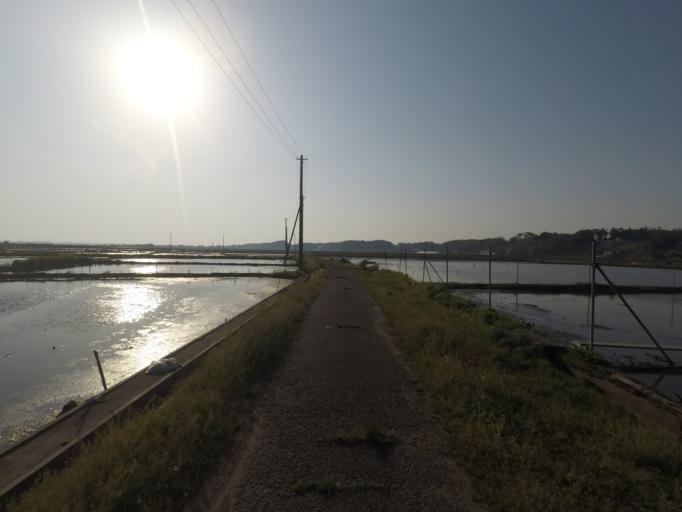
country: JP
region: Ibaraki
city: Ami
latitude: 36.0687
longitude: 140.2717
